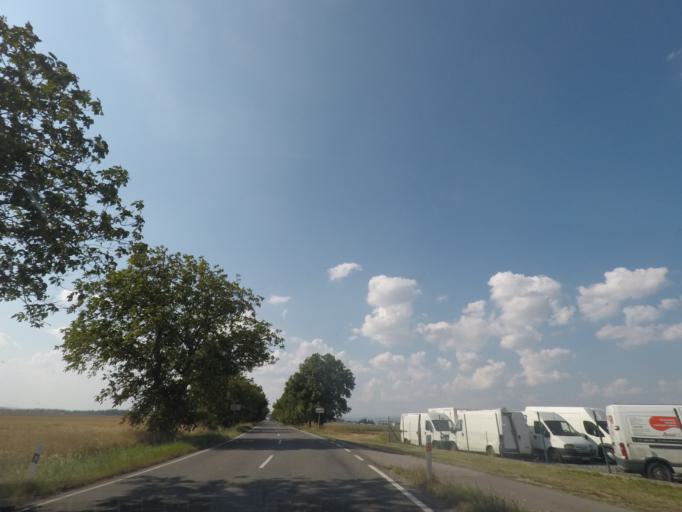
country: CZ
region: Kralovehradecky
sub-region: Okres Nachod
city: Jaromer
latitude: 50.3252
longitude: 15.9505
